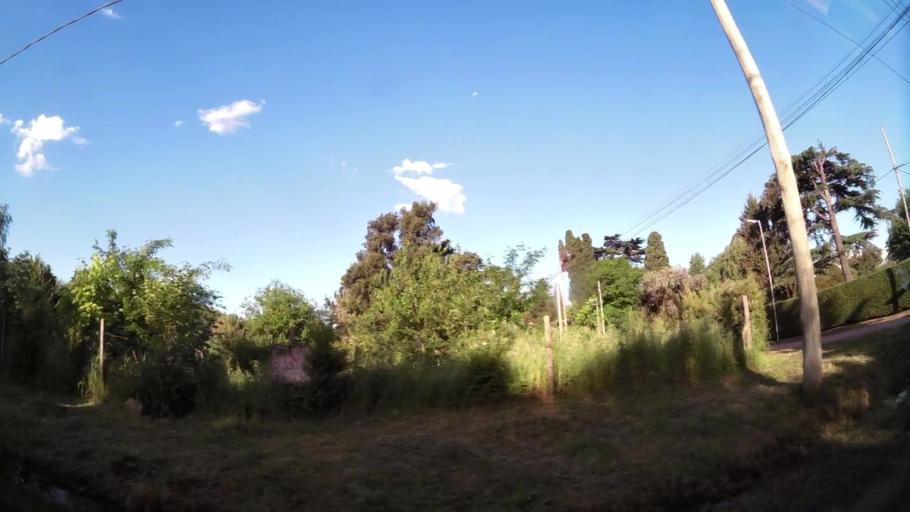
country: AR
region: Buenos Aires
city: Santa Catalina - Dique Lujan
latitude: -34.4670
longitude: -58.7455
